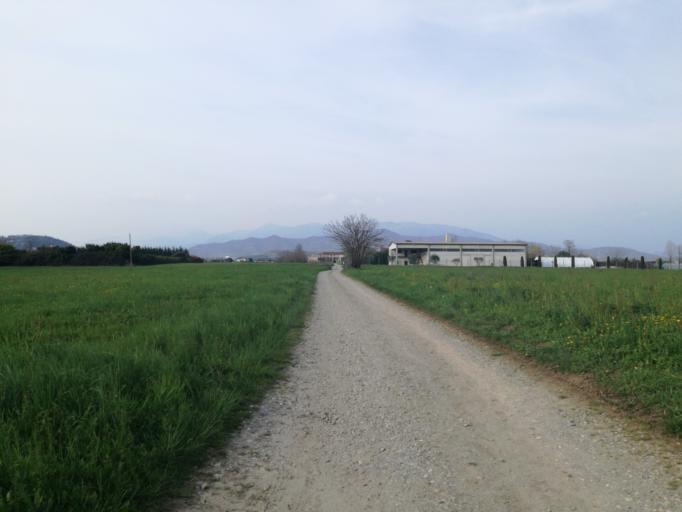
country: IT
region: Lombardy
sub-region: Provincia di Lecco
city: Verderio Superiore
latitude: 45.6689
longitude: 9.4529
